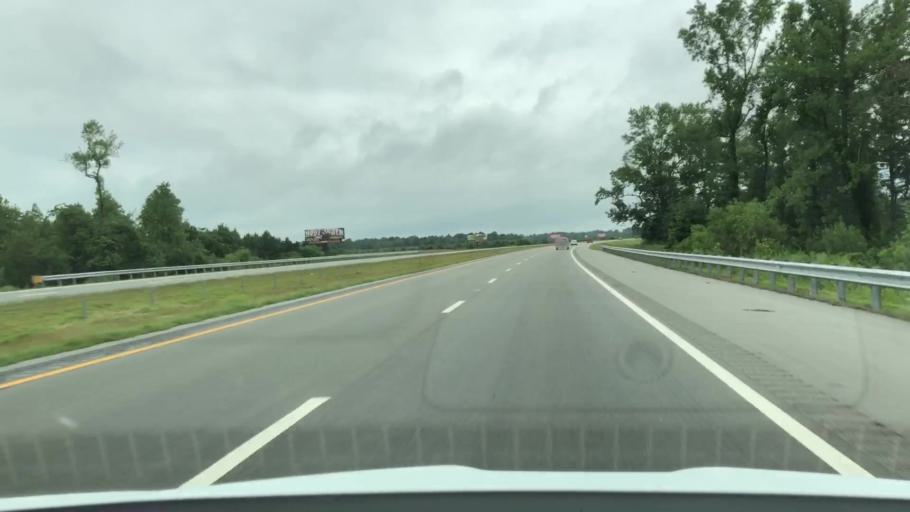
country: US
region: North Carolina
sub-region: Lenoir County
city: La Grange
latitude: 35.3214
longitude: -77.8356
